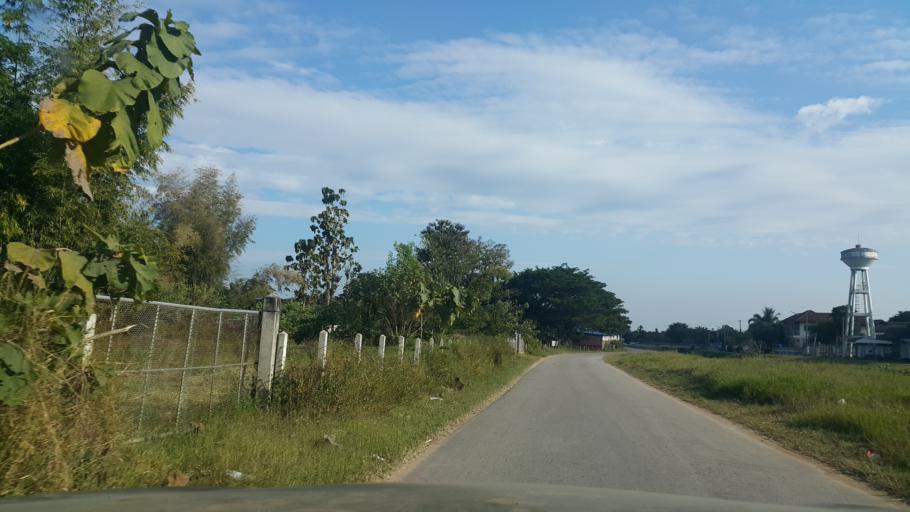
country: TH
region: Lampang
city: Hang Chat
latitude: 18.3157
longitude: 99.3489
